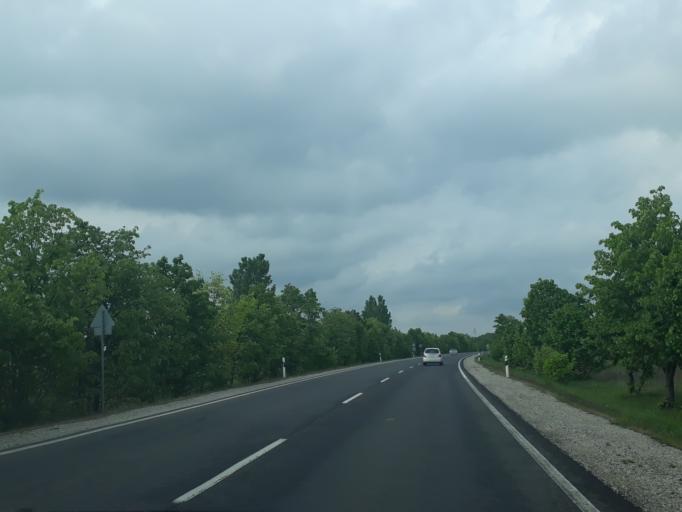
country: HU
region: Szabolcs-Szatmar-Bereg
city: Ajak
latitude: 48.1919
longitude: 22.0423
